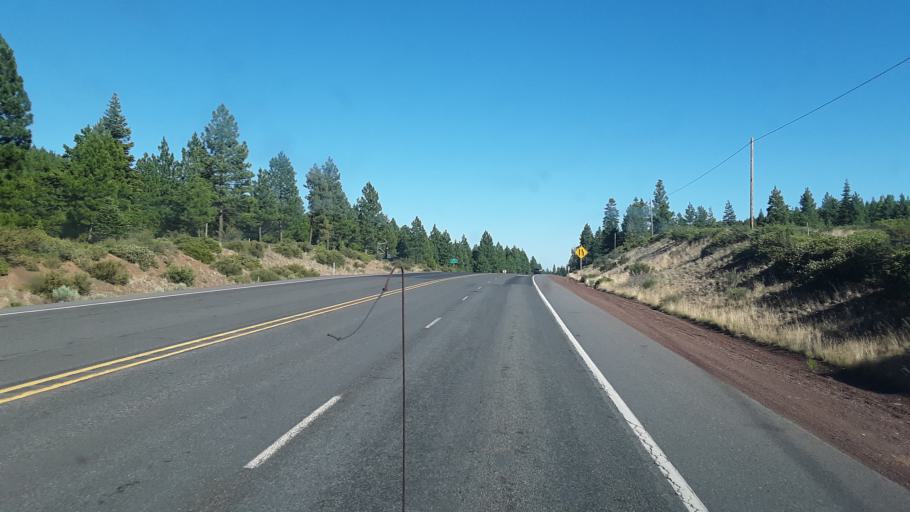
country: US
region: Oregon
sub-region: Klamath County
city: Klamath Falls
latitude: 42.3535
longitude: -121.9840
